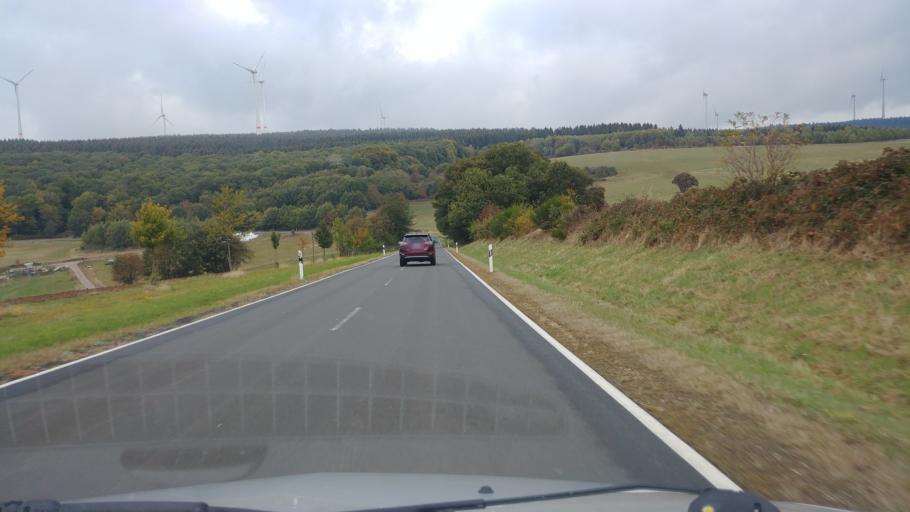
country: DE
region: Rheinland-Pfalz
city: Merschbach
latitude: 49.8192
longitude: 7.0333
